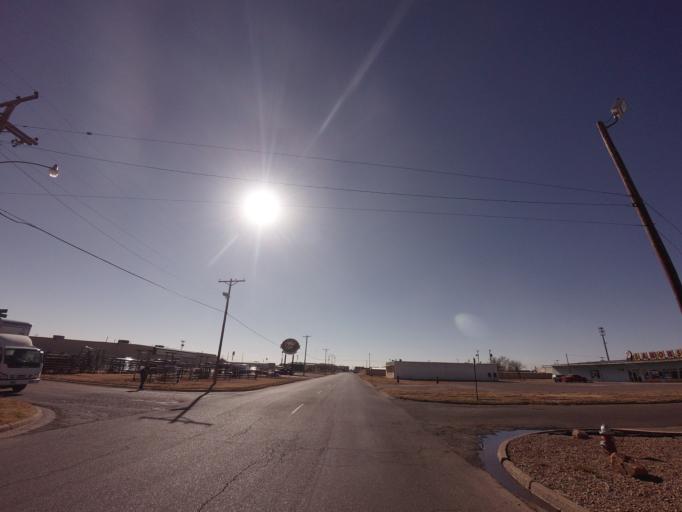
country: US
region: New Mexico
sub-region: Curry County
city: Clovis
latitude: 34.3999
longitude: -103.1877
